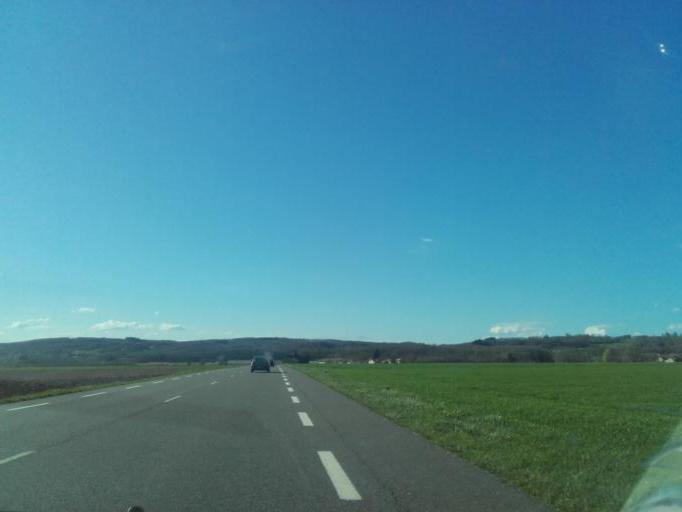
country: FR
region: Rhone-Alpes
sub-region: Departement de l'Isere
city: Champier
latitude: 45.4295
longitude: 5.3105
